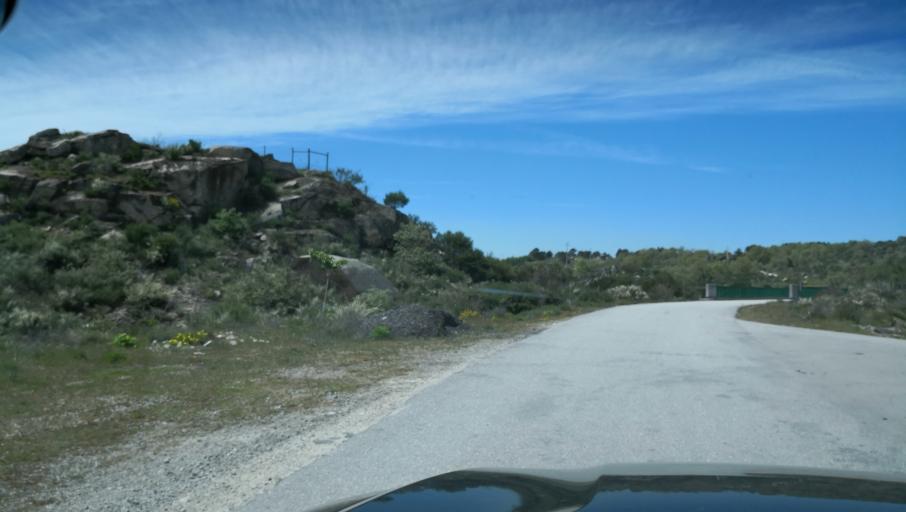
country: PT
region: Vila Real
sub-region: Vila Real
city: Vila Real
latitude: 41.3714
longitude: -7.6753
